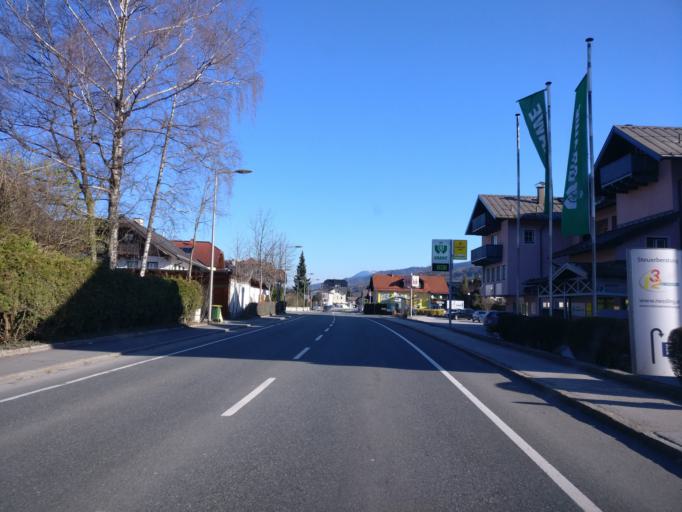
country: AT
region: Salzburg
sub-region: Politischer Bezirk Hallein
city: Oberalm
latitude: 47.6925
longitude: 13.1005
